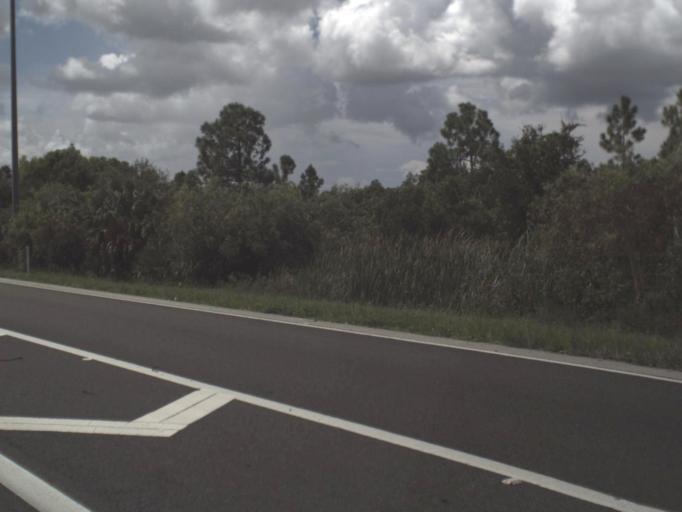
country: US
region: Florida
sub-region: Collier County
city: Vineyards
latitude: 26.2059
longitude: -81.7362
